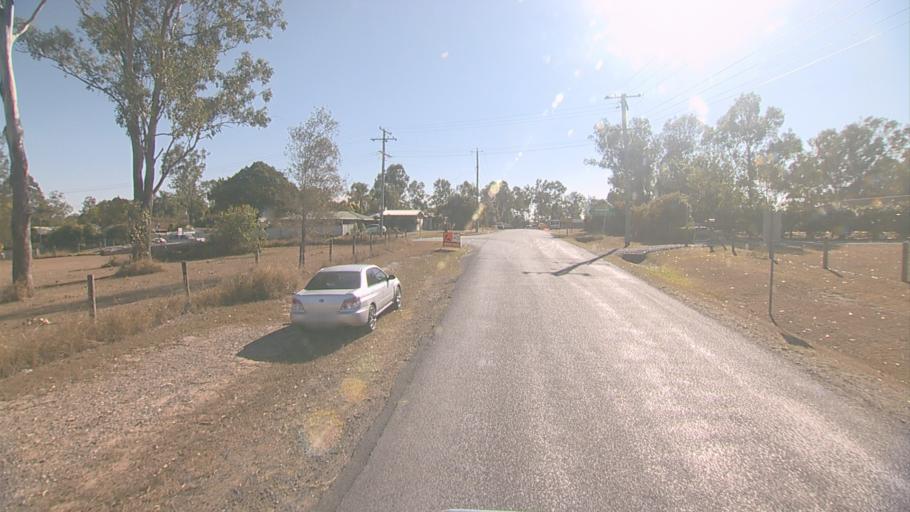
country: AU
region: Queensland
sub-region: Logan
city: Cedar Vale
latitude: -27.8360
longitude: 153.0319
